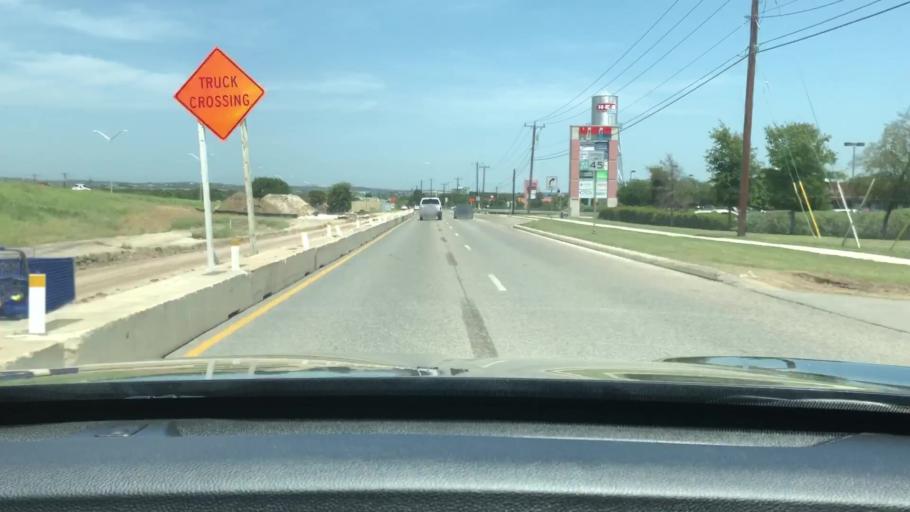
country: US
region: Texas
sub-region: Bexar County
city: Helotes
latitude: 29.5548
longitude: -98.6650
